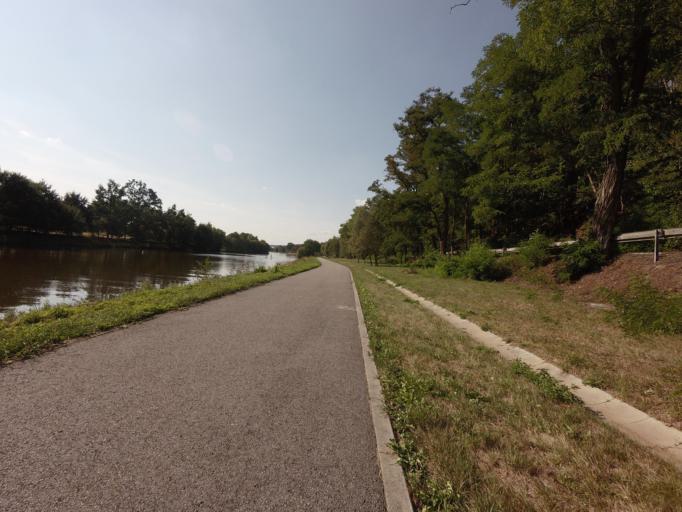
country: CZ
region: Jihocesky
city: Tyn nad Vltavou
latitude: 49.2130
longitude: 14.4399
